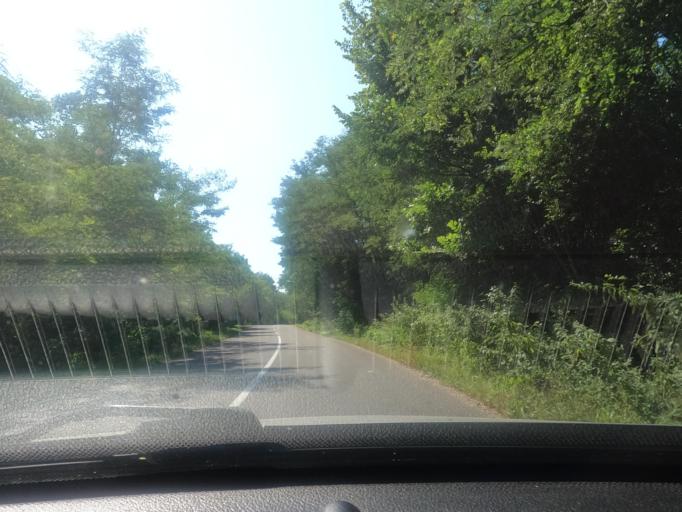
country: RS
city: Kozjak
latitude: 44.5452
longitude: 19.3013
